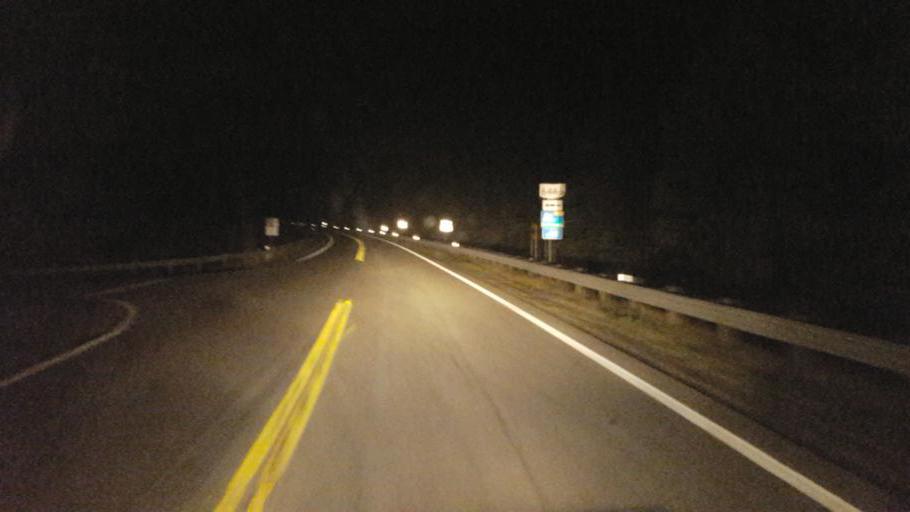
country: US
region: Ohio
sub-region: Harrison County
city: Cadiz
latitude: 40.3246
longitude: -81.1451
